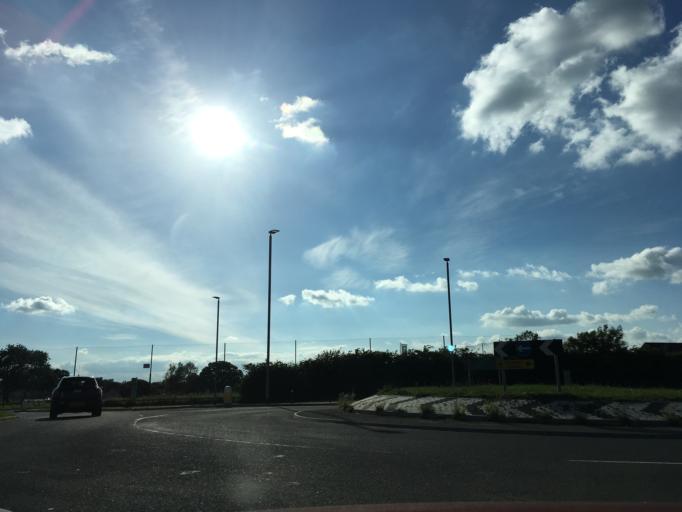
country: GB
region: England
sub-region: Somerset
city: Creech Saint Michael
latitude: 51.0388
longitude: -3.0531
